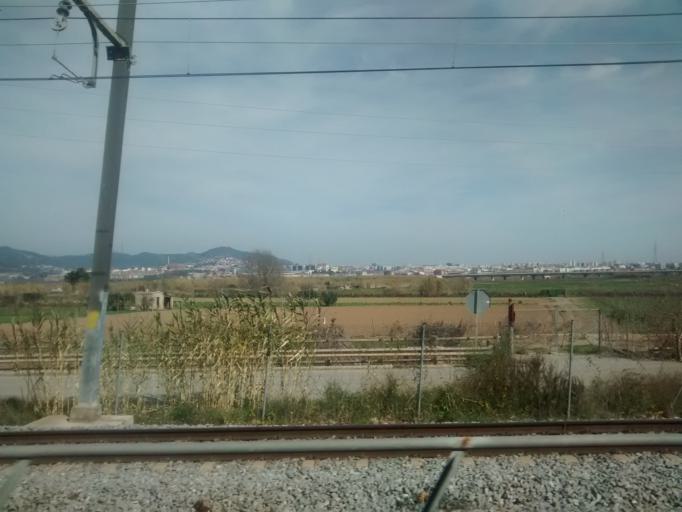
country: ES
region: Catalonia
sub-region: Provincia de Barcelona
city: Sant Boi de Llobregat
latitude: 41.3593
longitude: 2.0341
